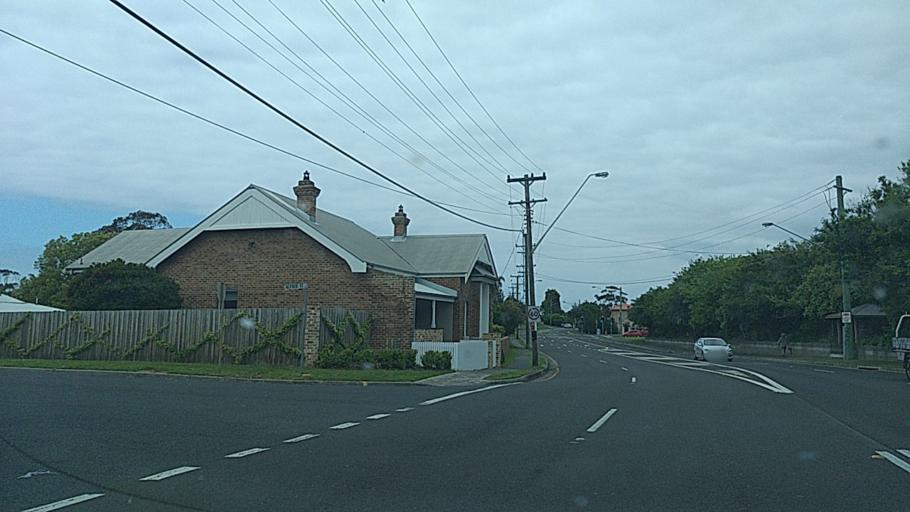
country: AU
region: New South Wales
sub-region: Wollongong
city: Bulli
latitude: -34.3471
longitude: 150.9039
